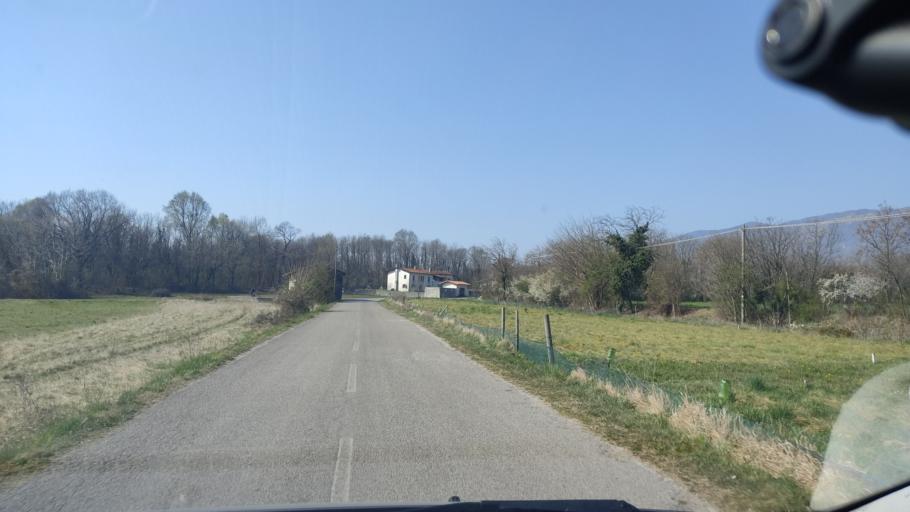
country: IT
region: Friuli Venezia Giulia
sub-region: Provincia di Pordenone
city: Budoia
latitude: 46.0503
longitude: 12.5498
